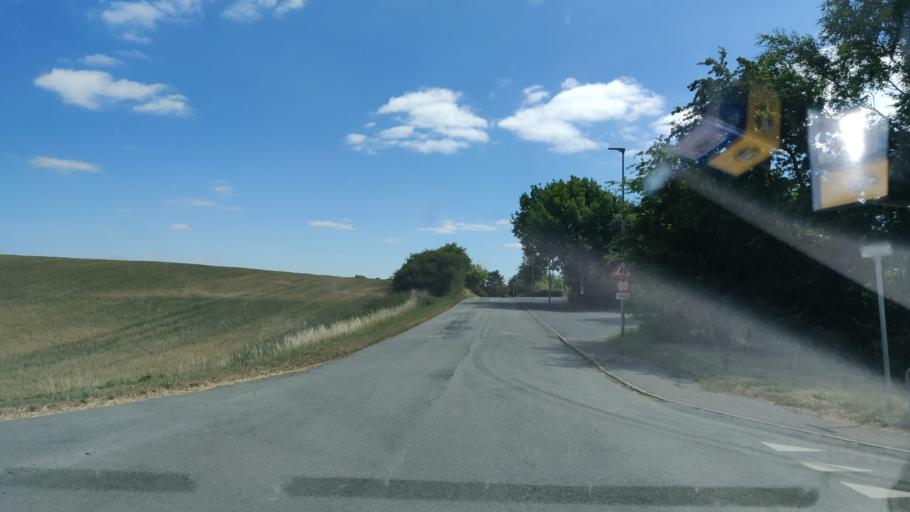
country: DK
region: South Denmark
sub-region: Kolding Kommune
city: Kolding
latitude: 55.5318
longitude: 9.5341
